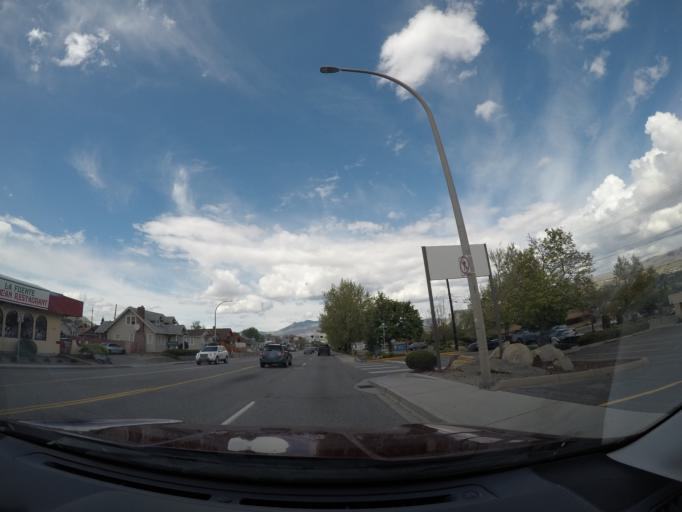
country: US
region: Washington
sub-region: Douglas County
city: East Wenatchee
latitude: 47.4121
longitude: -120.3039
